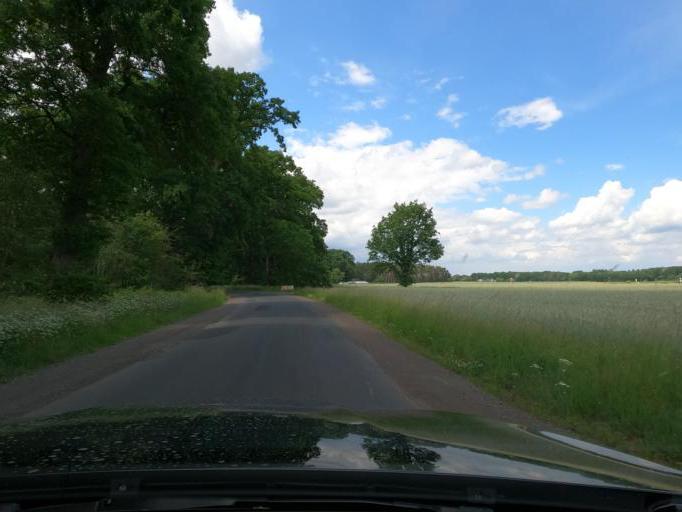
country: DE
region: Lower Saxony
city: Schwarmstedt
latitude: 52.6576
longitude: 9.6220
